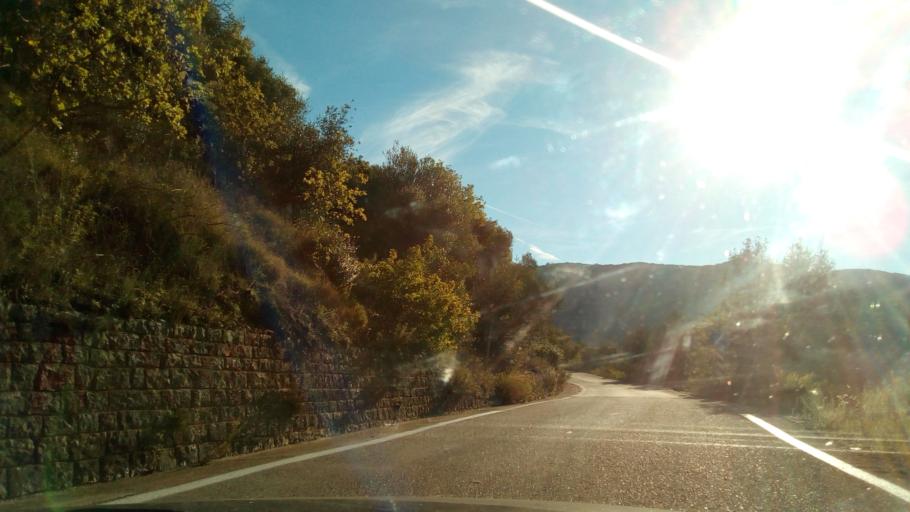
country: GR
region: West Greece
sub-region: Nomos Aitolias kai Akarnanias
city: Nafpaktos
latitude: 38.4690
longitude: 21.8782
